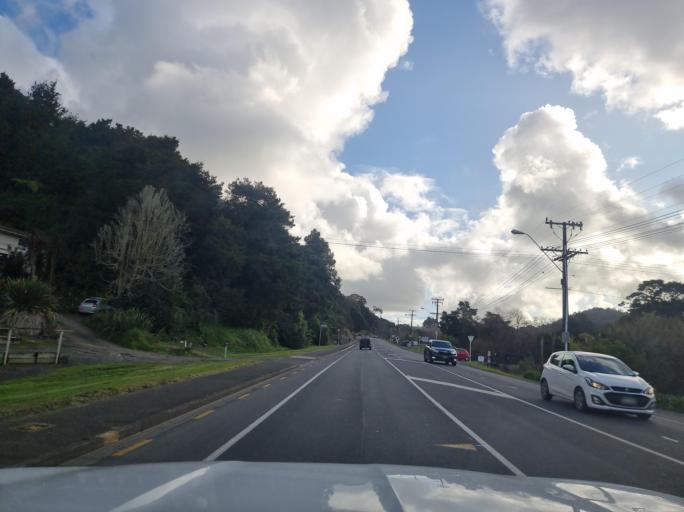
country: NZ
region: Northland
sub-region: Whangarei
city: Whangarei
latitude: -35.7345
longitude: 174.2898
